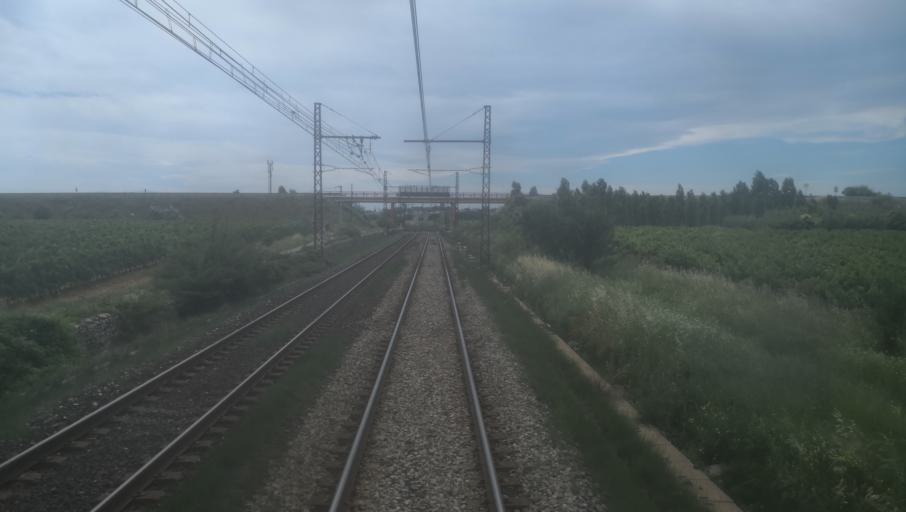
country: FR
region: Languedoc-Roussillon
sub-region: Departement de l'Herault
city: Vendargues
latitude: 43.6467
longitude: 3.9889
